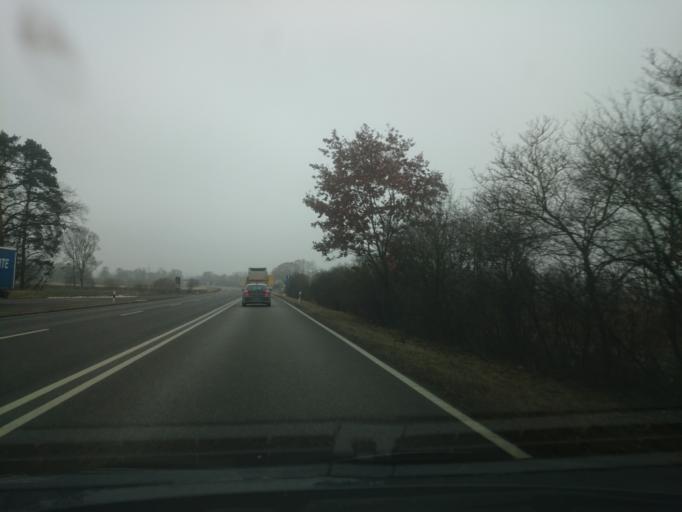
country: DE
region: Bavaria
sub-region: Upper Bavaria
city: Reichertshofen
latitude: 48.6497
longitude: 11.4862
